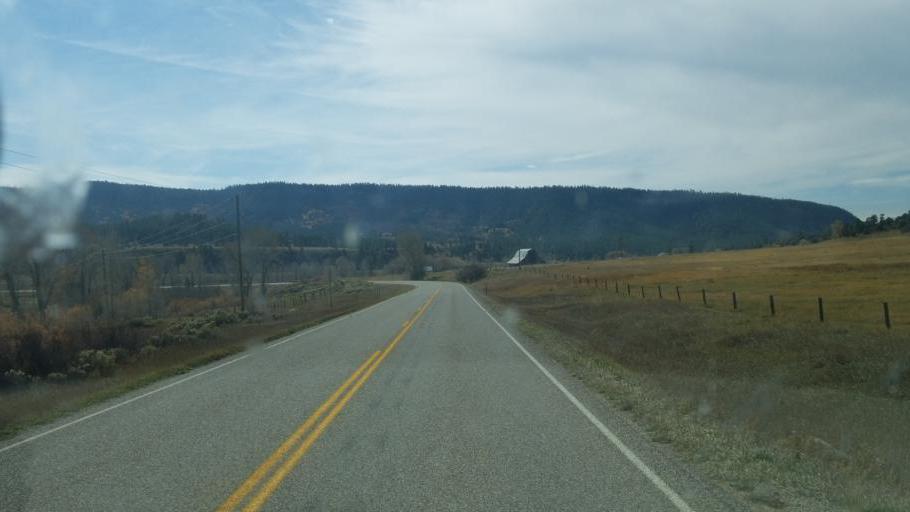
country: US
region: New Mexico
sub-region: Rio Arriba County
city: Dulce
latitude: 37.0405
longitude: -106.8441
